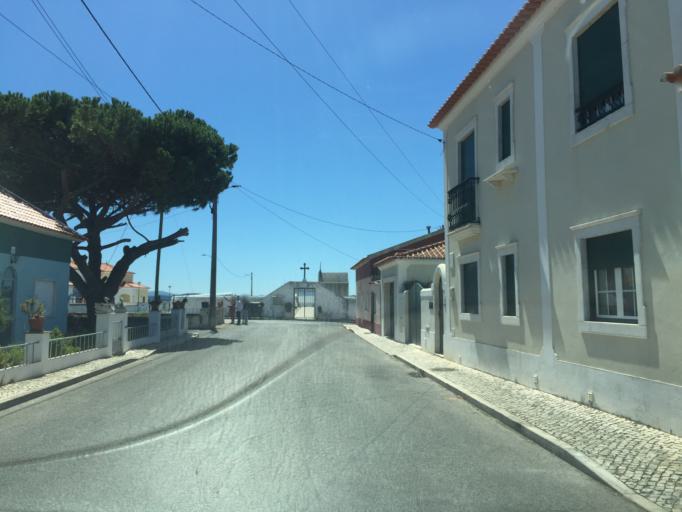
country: PT
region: Lisbon
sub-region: Torres Vedras
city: A dos Cunhados
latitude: 39.1758
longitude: -9.3161
